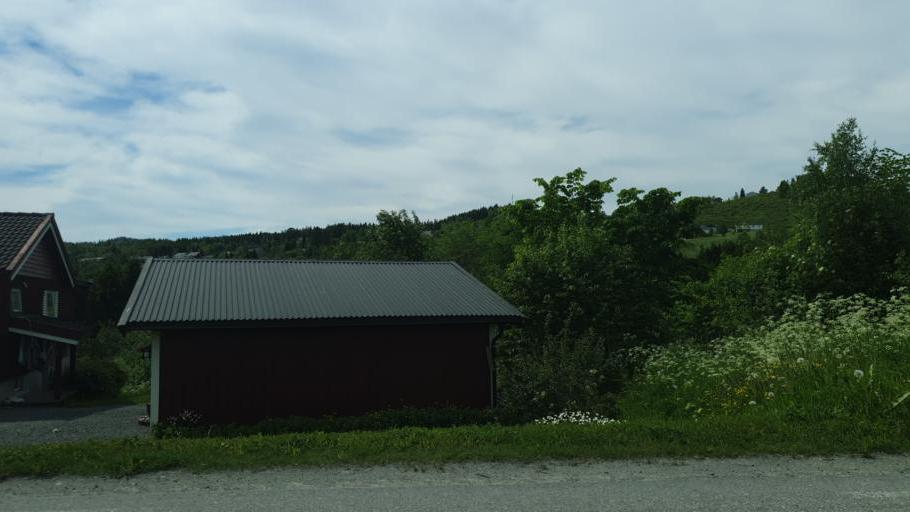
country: NO
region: Nord-Trondelag
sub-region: Leksvik
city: Leksvik
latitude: 63.6717
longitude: 10.6083
